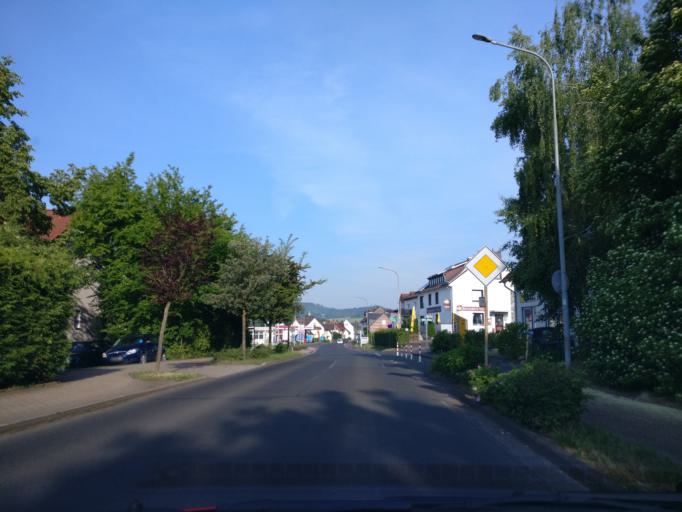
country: DE
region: Hesse
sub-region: Regierungsbezirk Kassel
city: Baunatal
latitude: 51.2728
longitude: 9.3850
